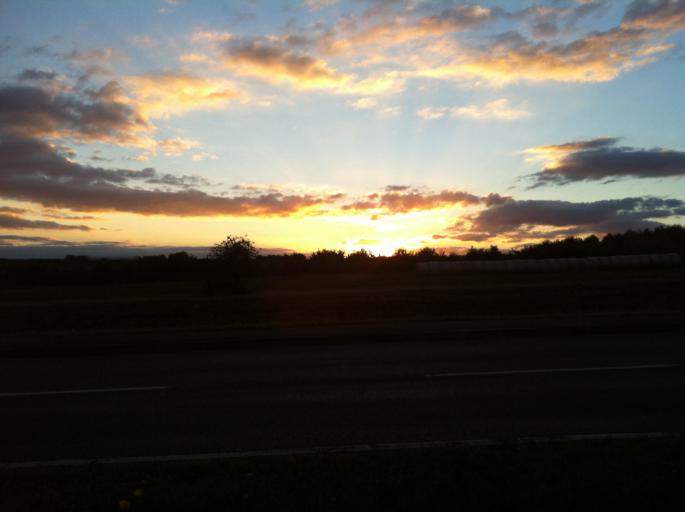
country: DE
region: Rheinland-Pfalz
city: Ober-Olm
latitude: 49.9789
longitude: 8.1874
